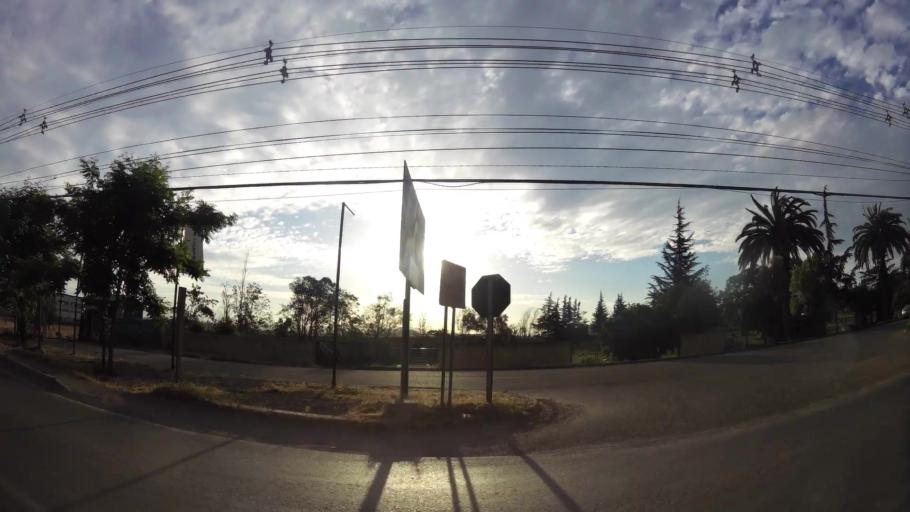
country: CL
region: Santiago Metropolitan
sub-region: Provincia de Maipo
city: San Bernardo
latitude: -33.6233
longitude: -70.6808
